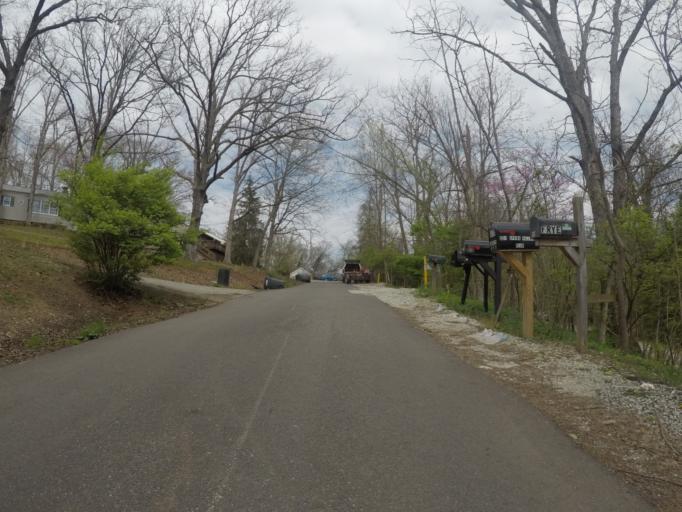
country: US
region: Ohio
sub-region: Lawrence County
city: Burlington
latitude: 38.3851
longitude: -82.5124
